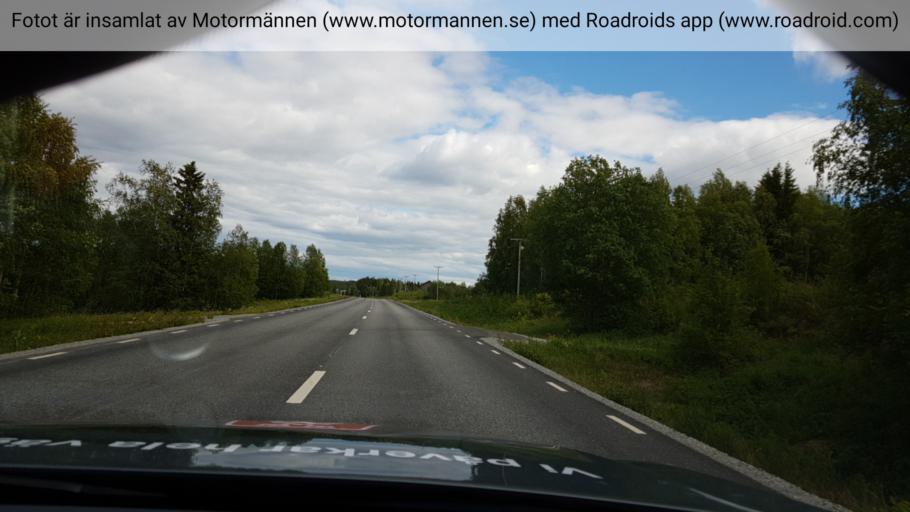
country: SE
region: Jaemtland
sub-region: Stroemsunds Kommun
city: Stroemsund
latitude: 64.2172
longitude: 15.5540
